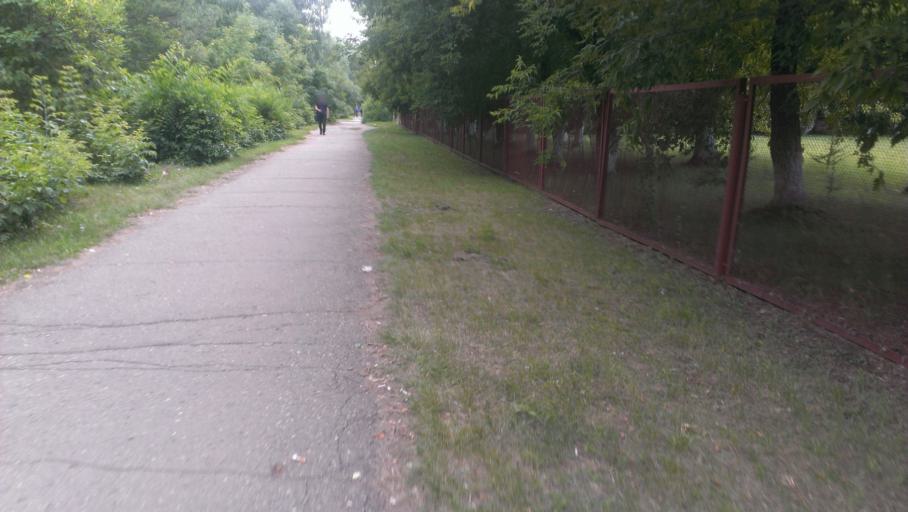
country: RU
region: Altai Krai
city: Yuzhnyy
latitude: 53.2517
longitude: 83.6942
